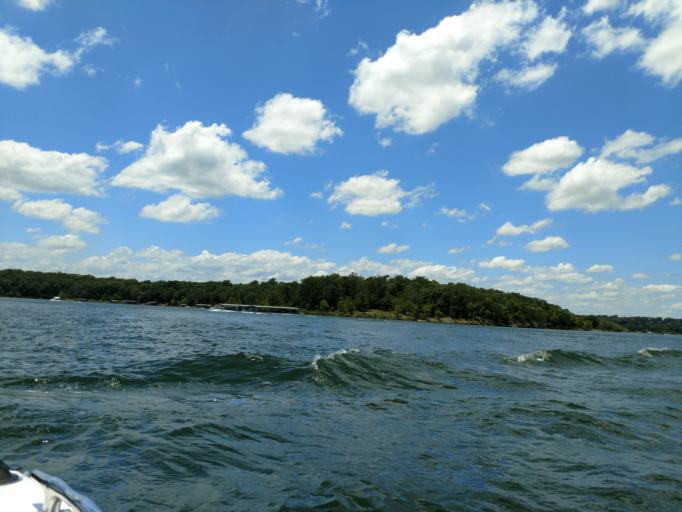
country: US
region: Missouri
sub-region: Barry County
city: Shell Knob
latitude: 36.5868
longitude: -93.5650
